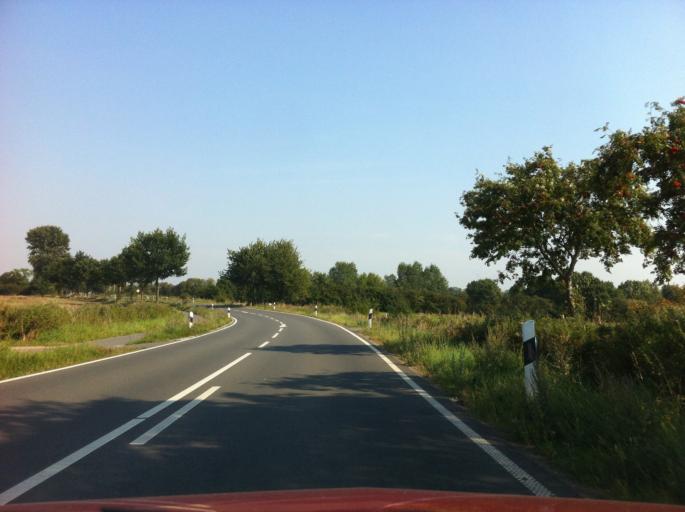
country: DE
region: Schleswig-Holstein
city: Harmsdorf
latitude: 54.3043
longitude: 10.8367
